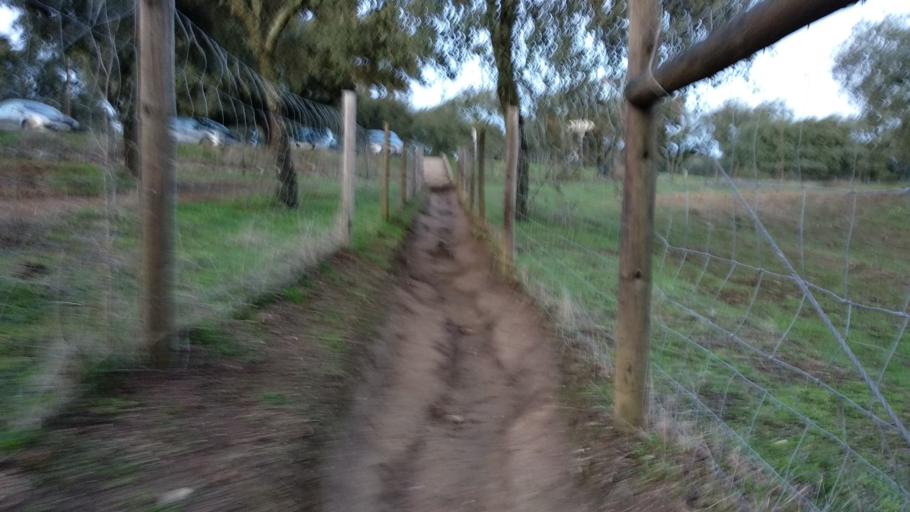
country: PT
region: Evora
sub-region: Evora
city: Evora
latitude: 38.5657
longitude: -8.0464
